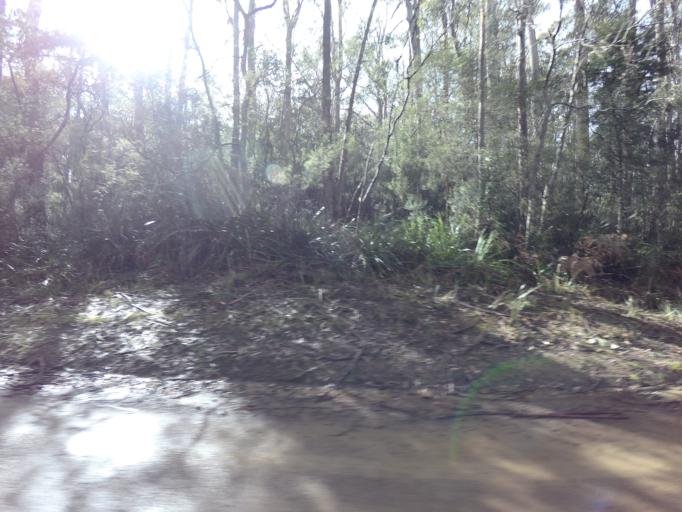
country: AU
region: Tasmania
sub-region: Huon Valley
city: Geeveston
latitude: -43.5705
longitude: 146.8893
